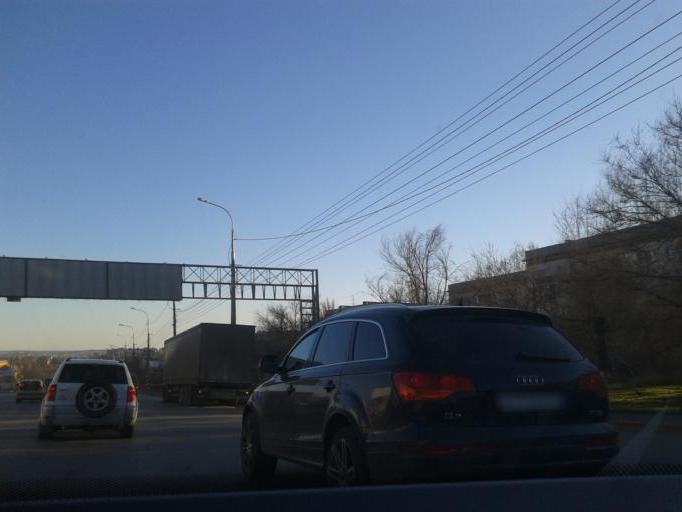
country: RU
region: Volgograd
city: Volgograd
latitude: 48.6648
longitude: 44.4401
